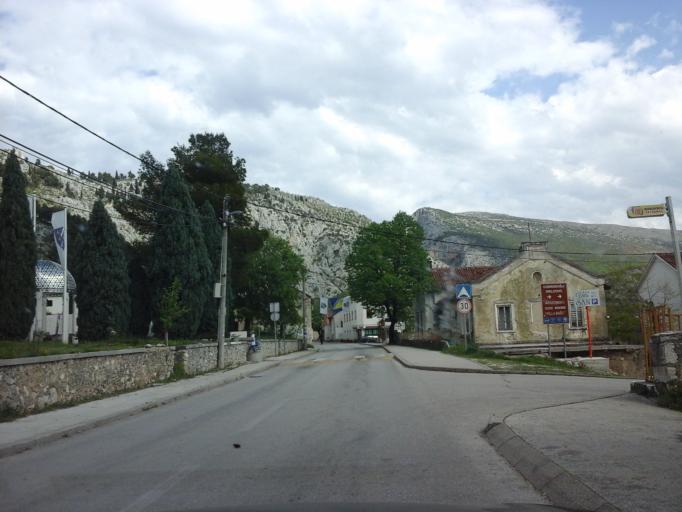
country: BA
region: Federation of Bosnia and Herzegovina
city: Blagaj
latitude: 43.2576
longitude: 17.8926
